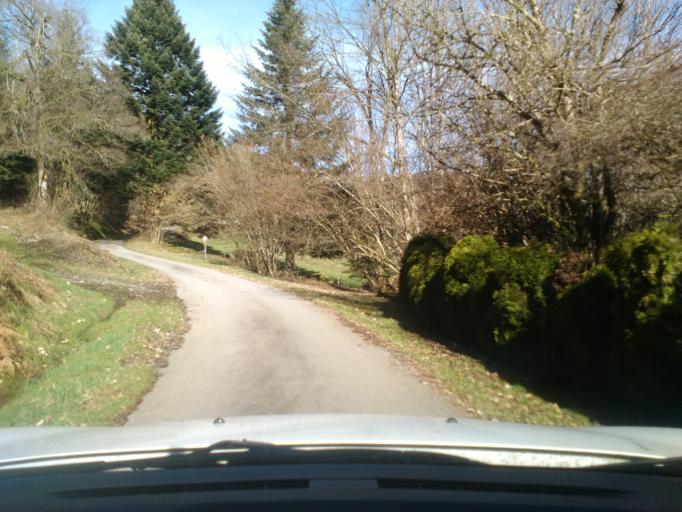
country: FR
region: Lorraine
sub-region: Departement des Vosges
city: Saint-Ame
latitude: 48.0477
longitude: 6.6721
